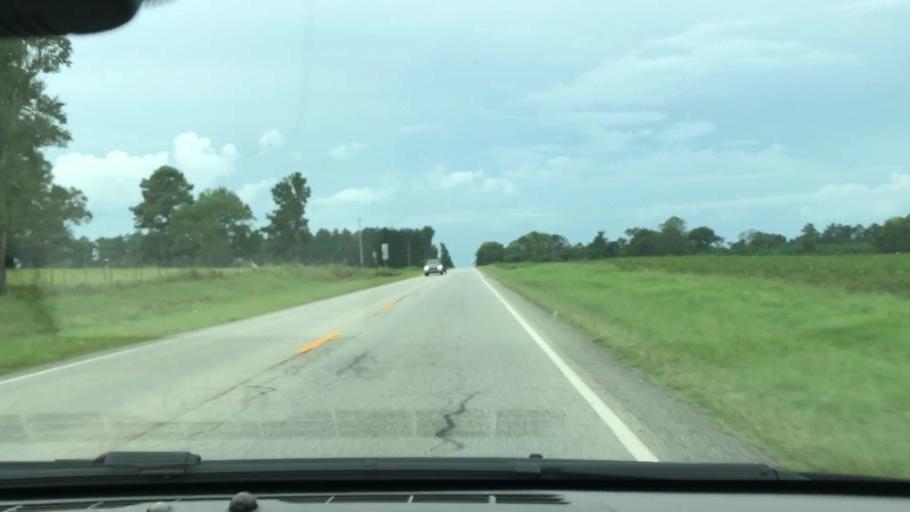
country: US
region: Georgia
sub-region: Early County
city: Blakely
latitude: 31.3288
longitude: -85.0054
